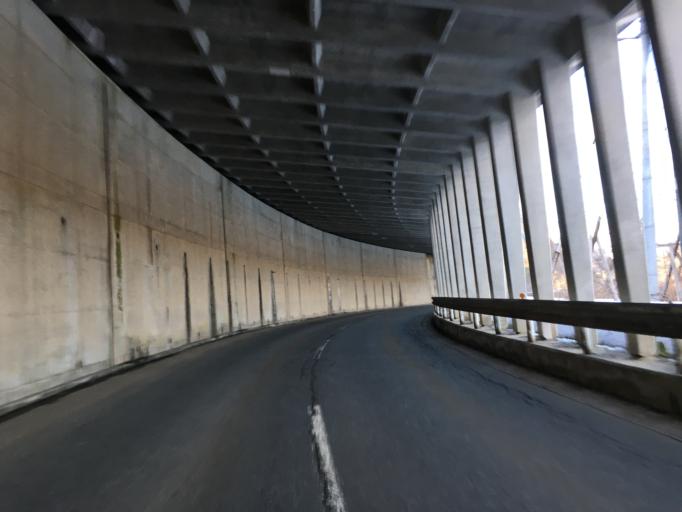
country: JP
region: Yamagata
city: Nagai
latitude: 37.9540
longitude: 139.9166
